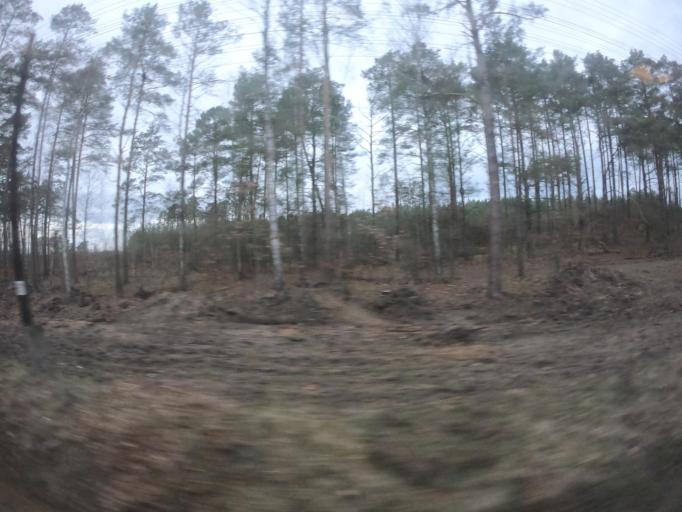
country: PL
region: West Pomeranian Voivodeship
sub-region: Powiat szczecinecki
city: Lubowo
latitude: 53.6011
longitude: 16.4330
